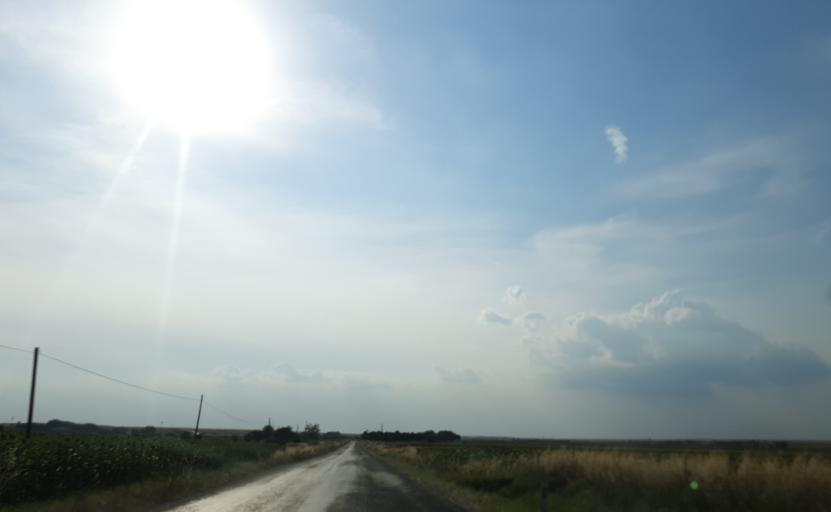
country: TR
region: Tekirdag
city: Muratli
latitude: 41.2142
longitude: 27.4404
